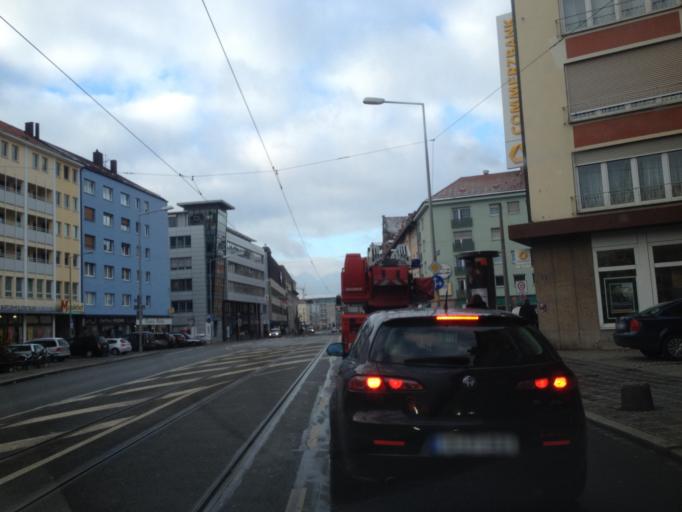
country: DE
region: Bavaria
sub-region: Regierungsbezirk Mittelfranken
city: Nuernberg
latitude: 49.4589
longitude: 11.0970
